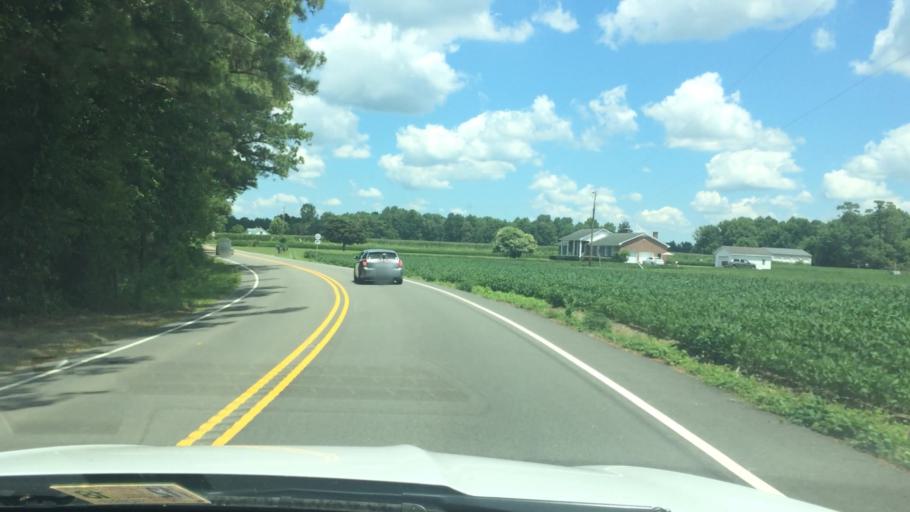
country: US
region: Virginia
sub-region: King William County
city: West Point
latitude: 37.5972
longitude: -76.7647
